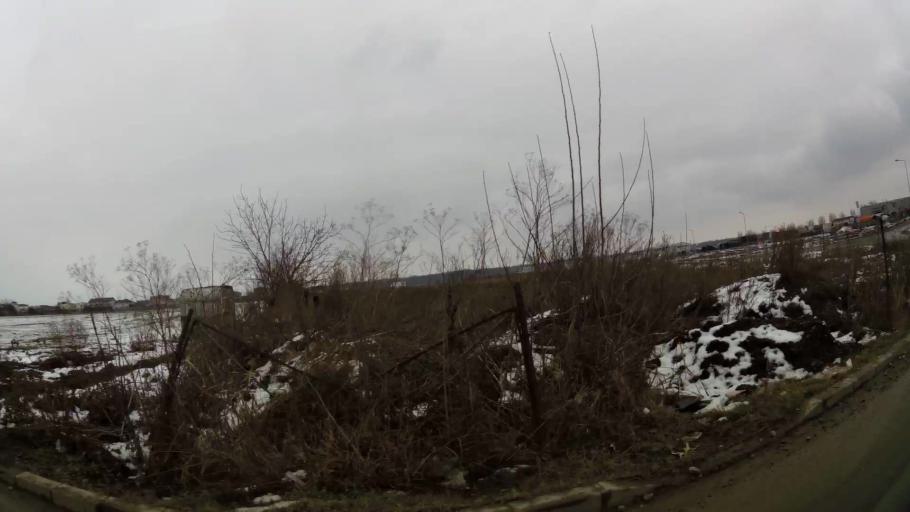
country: RO
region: Ilfov
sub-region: Comuna Otopeni
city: Otopeni
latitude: 44.5483
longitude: 26.0925
